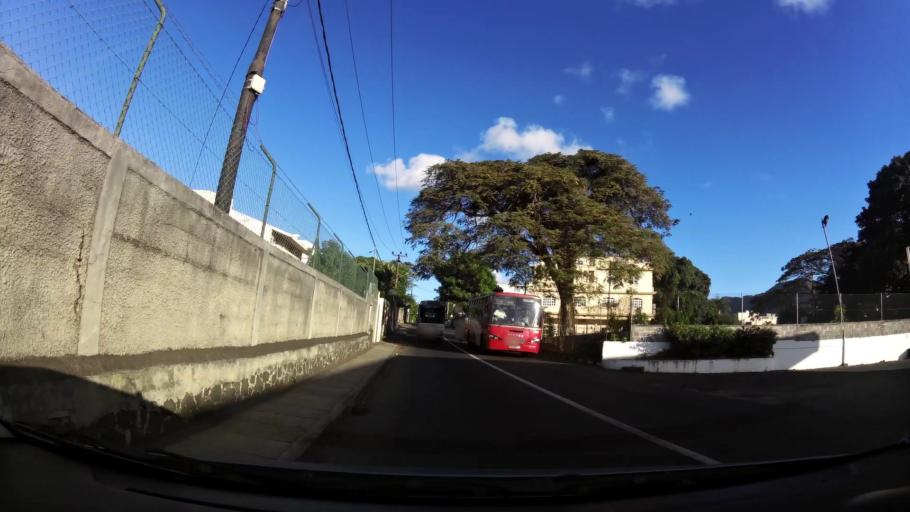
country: MU
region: Plaines Wilhems
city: Ebene
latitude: -20.2365
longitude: 57.4629
